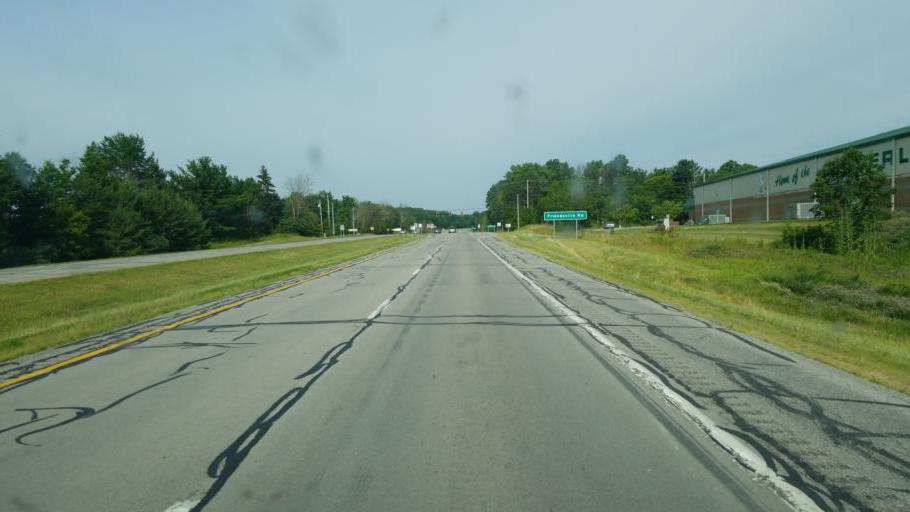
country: US
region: Ohio
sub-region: Medina County
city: Westfield Center
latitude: 41.0387
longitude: -81.9635
